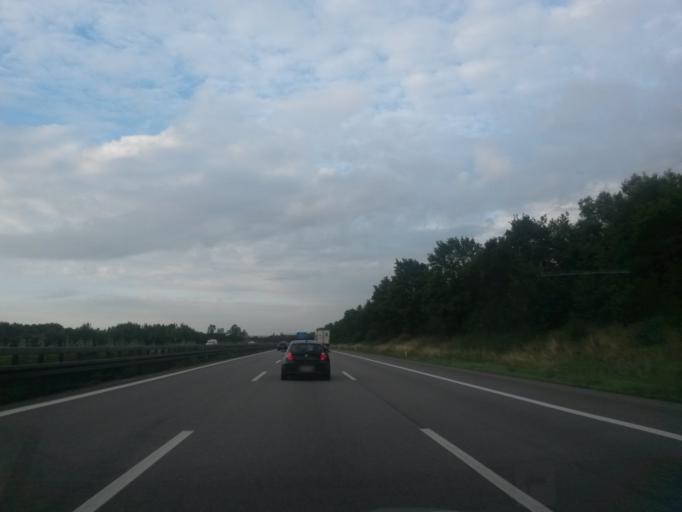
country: DE
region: Bavaria
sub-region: Upper Bavaria
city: Lenting
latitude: 48.7914
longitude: 11.4613
